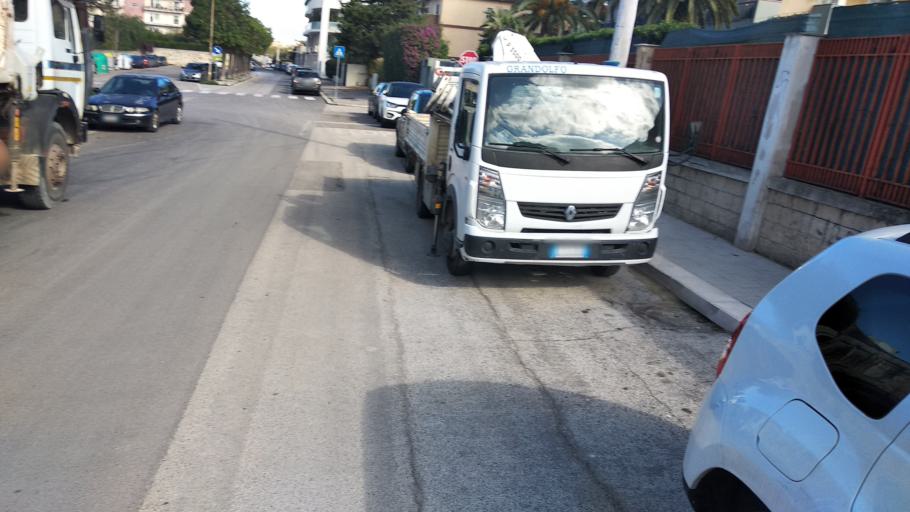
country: IT
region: Apulia
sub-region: Provincia di Bari
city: Bari
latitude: 41.1114
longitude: 16.8549
